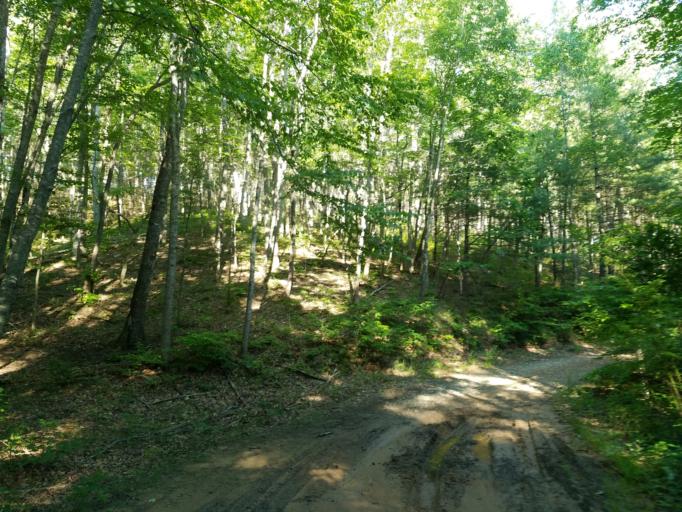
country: US
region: Georgia
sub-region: Fannin County
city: Blue Ridge
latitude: 34.8040
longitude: -84.1752
